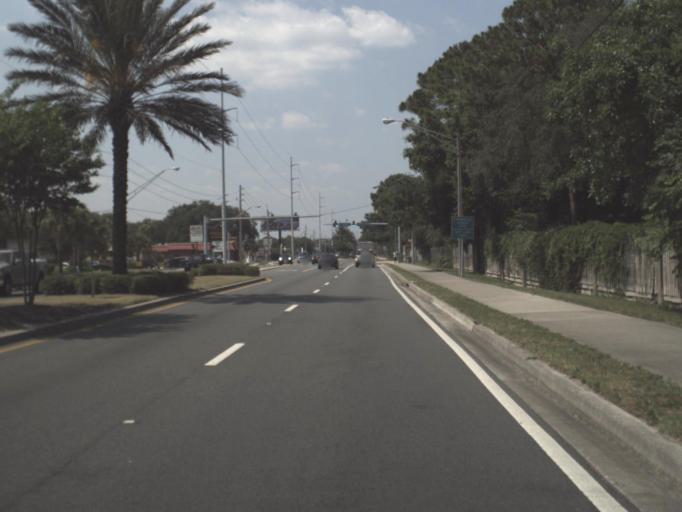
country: US
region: Florida
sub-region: Duval County
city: Atlantic Beach
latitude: 30.3453
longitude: -81.4133
